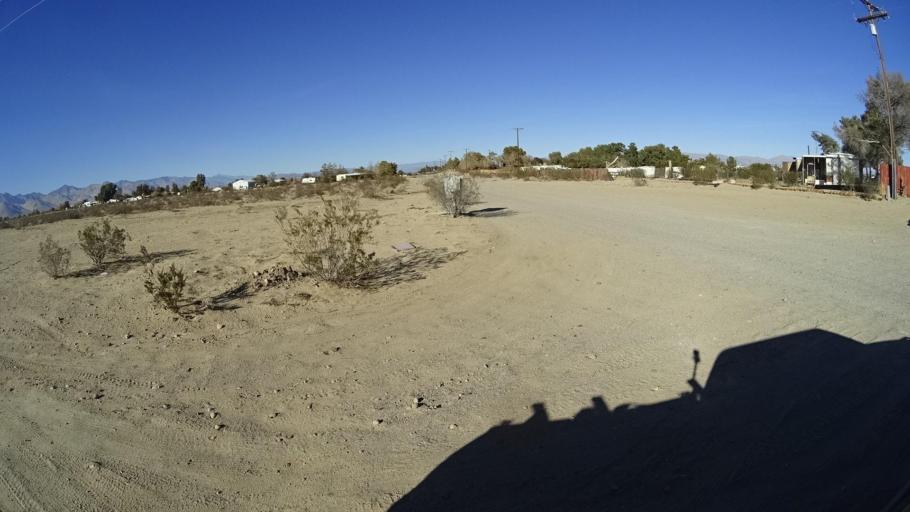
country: US
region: California
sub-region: Kern County
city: China Lake Acres
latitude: 35.6369
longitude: -117.7587
